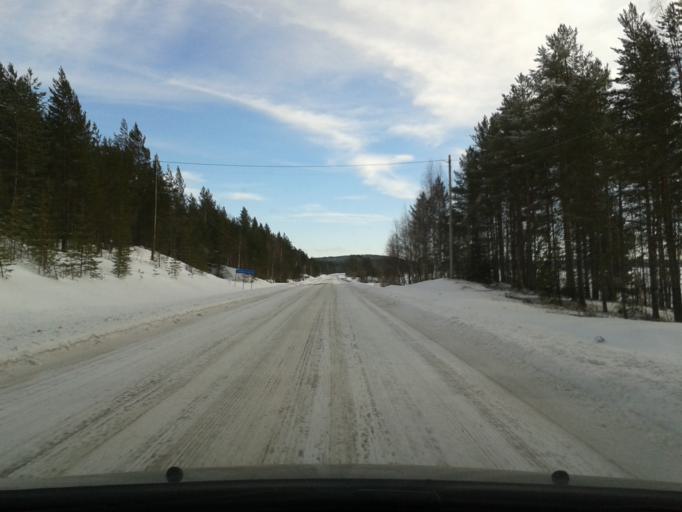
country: SE
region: Vaesterbotten
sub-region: Vilhelmina Kommun
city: Vilhelmina
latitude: 64.3911
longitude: 16.8723
